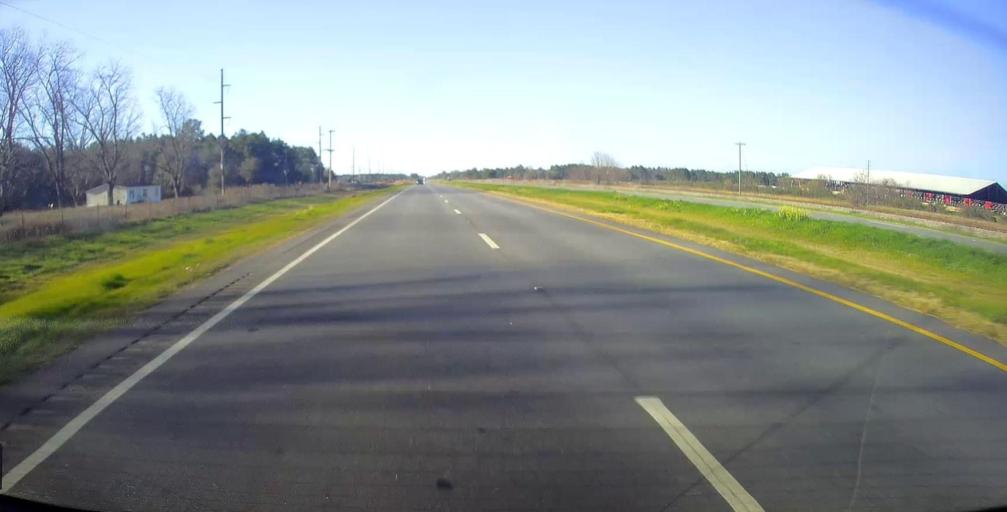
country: US
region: Georgia
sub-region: Lee County
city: Leesburg
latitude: 31.7848
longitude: -84.1972
